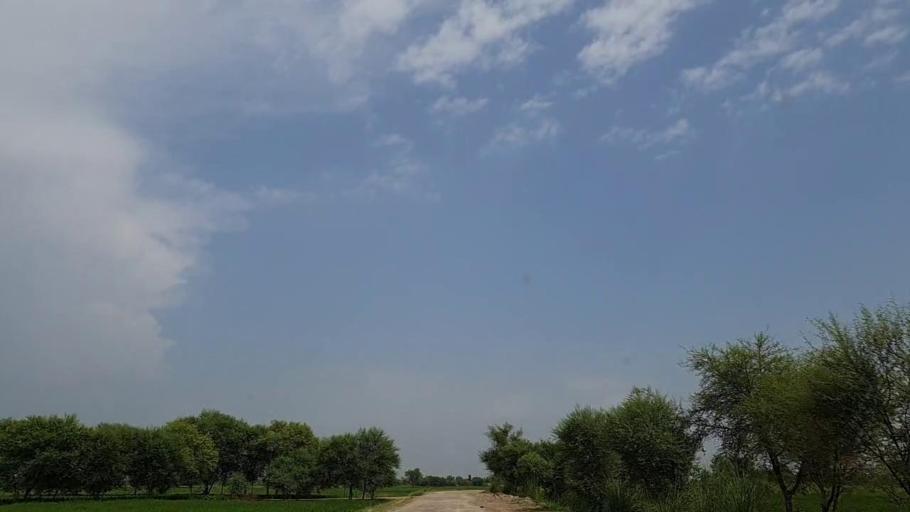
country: PK
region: Sindh
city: Khanpur
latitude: 27.8433
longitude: 69.4635
